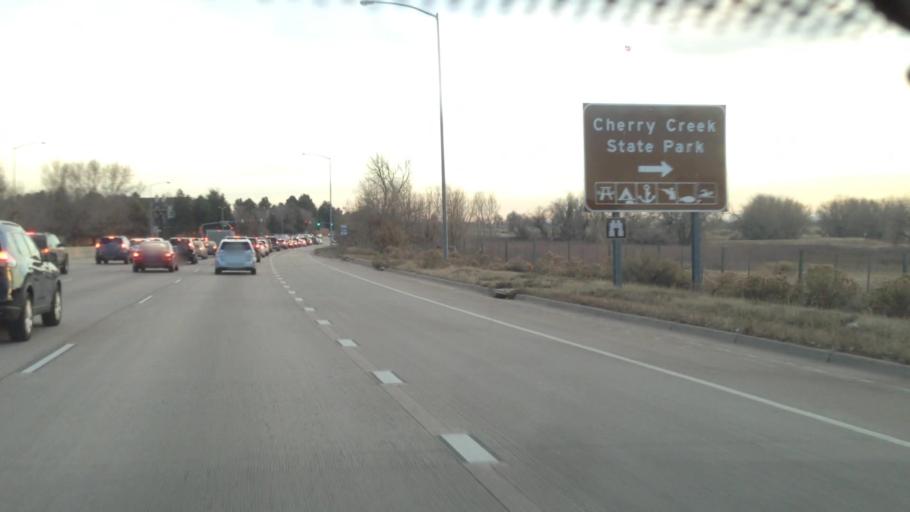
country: US
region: Colorado
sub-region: Arapahoe County
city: Dove Valley
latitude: 39.6497
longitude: -104.8296
